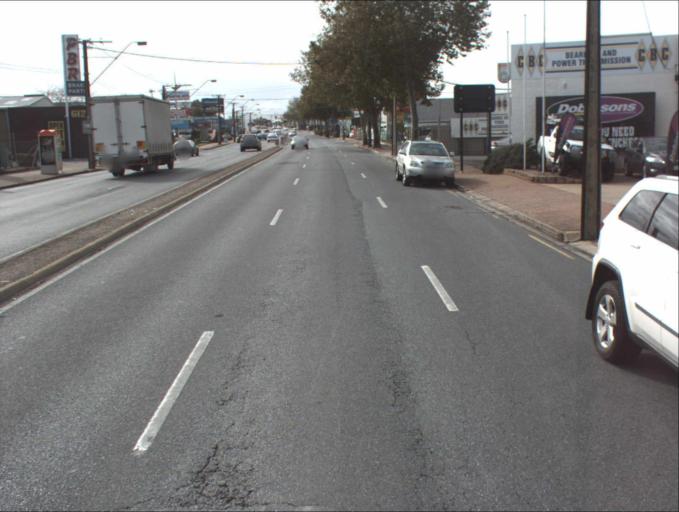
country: AU
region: South Australia
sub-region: Port Adelaide Enfield
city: Gilles Plains
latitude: -34.8553
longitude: 138.6595
